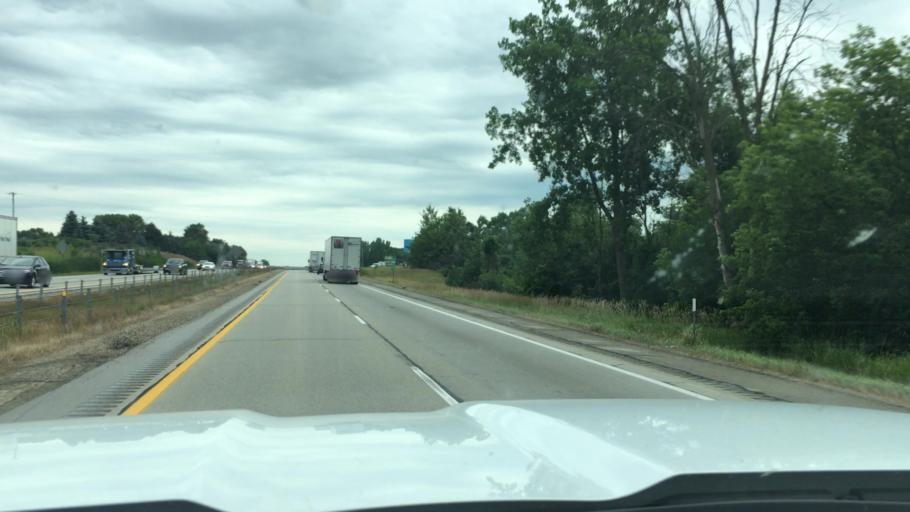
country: US
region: Michigan
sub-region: Allegan County
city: Wayland
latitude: 42.6825
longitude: -85.6608
